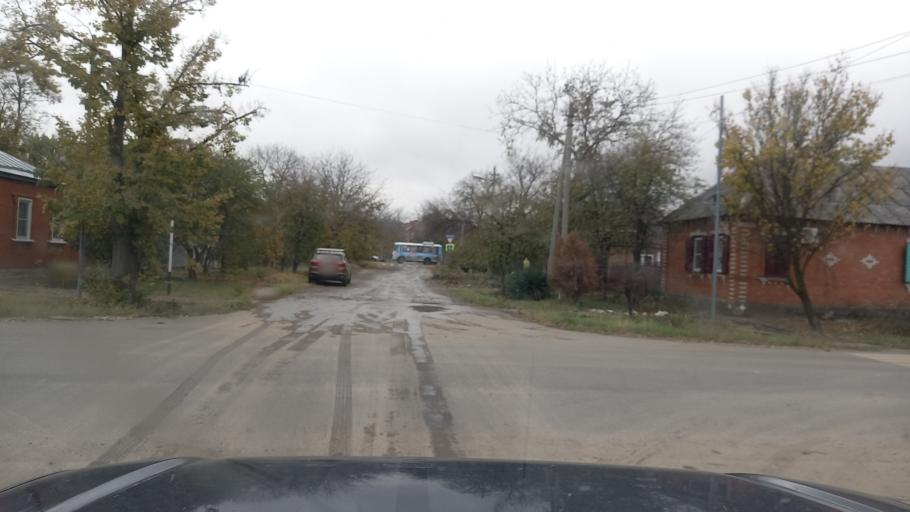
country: RU
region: Adygeya
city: Maykop
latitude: 44.6031
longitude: 40.0855
